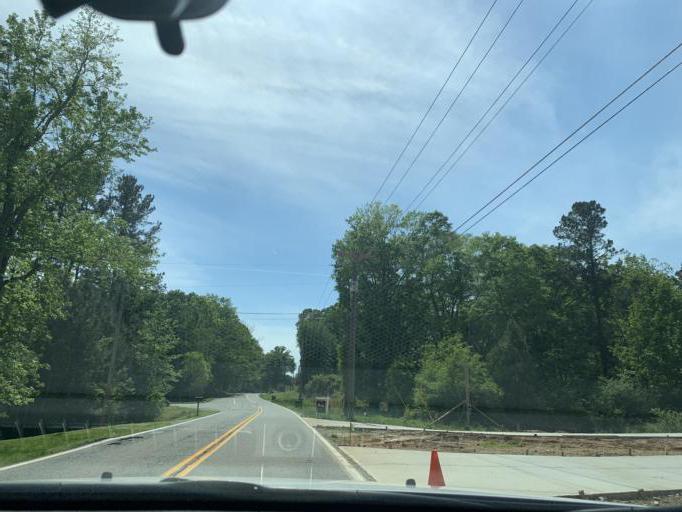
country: US
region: Georgia
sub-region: Forsyth County
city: Cumming
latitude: 34.2621
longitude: -84.1916
